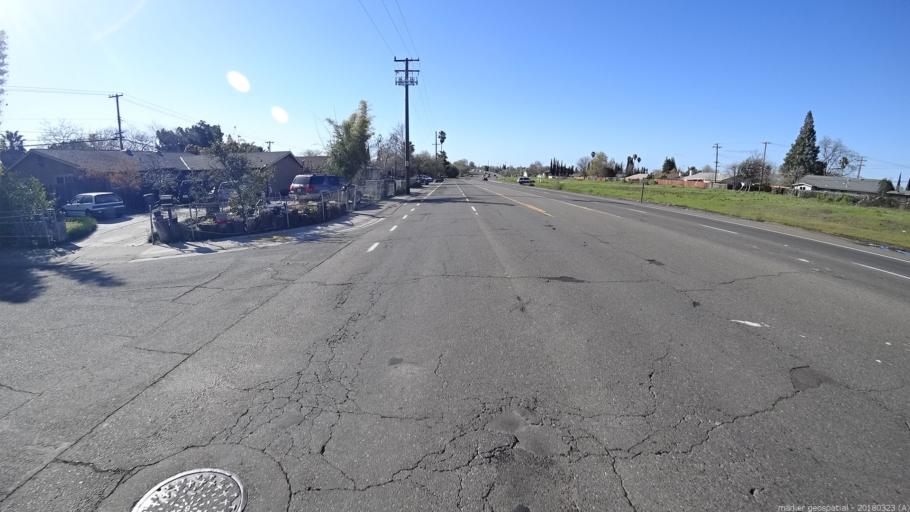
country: US
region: California
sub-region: Sacramento County
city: North Highlands
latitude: 38.6835
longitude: -121.3637
